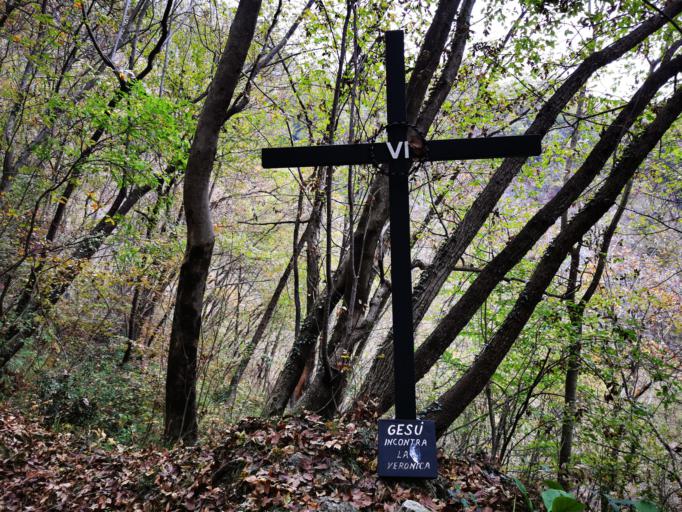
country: IT
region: Lombardy
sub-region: Provincia di Lecco
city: Mandello del Lario
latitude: 45.9340
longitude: 9.3345
